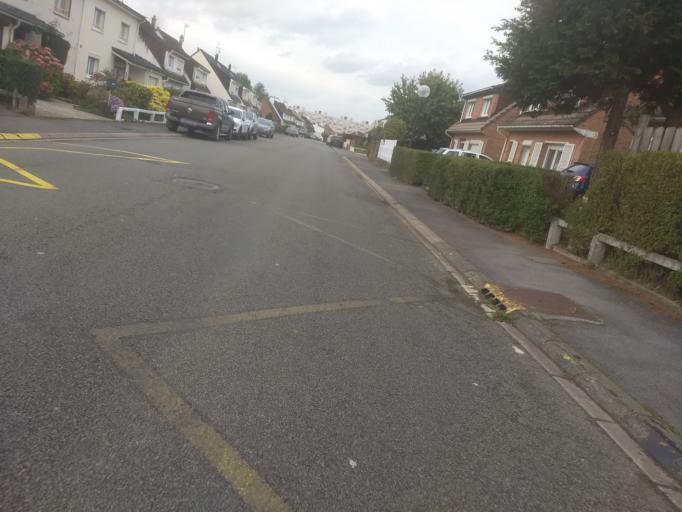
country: FR
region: Nord-Pas-de-Calais
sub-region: Departement du Pas-de-Calais
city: Agny
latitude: 50.2680
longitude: 2.7710
